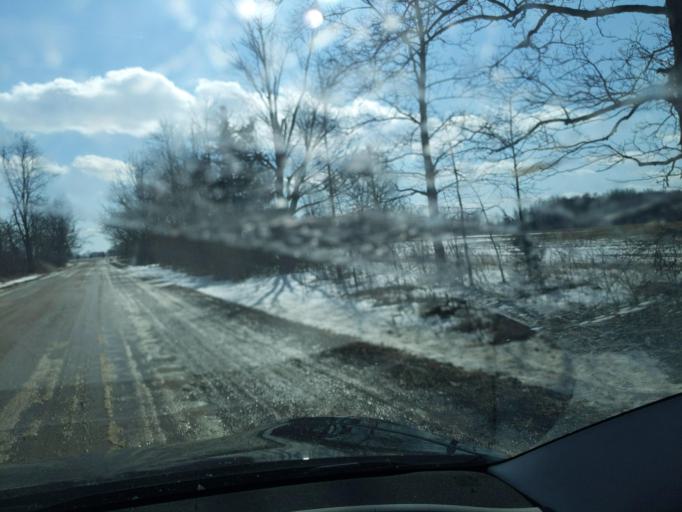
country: US
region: Michigan
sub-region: Livingston County
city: Fowlerville
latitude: 42.6016
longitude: -84.0906
